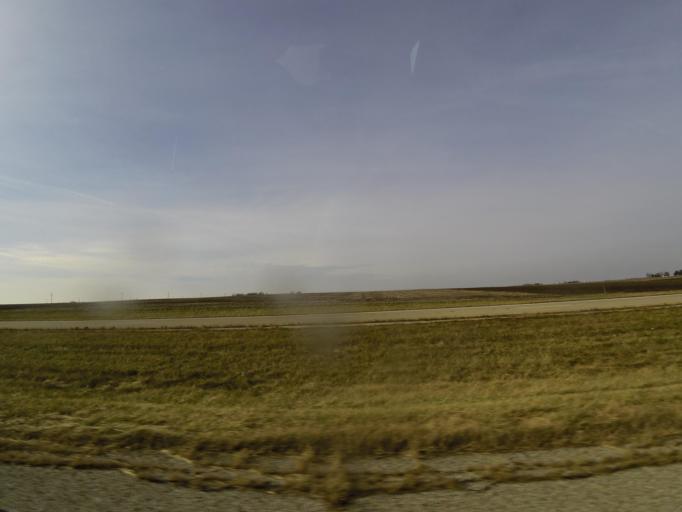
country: US
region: Illinois
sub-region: McLean County
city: Heyworth
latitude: 40.3632
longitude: -88.9893
